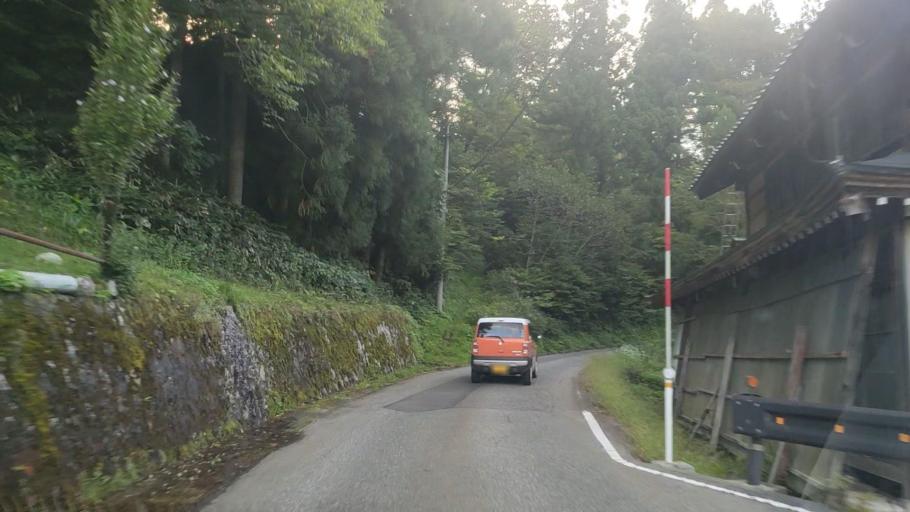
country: JP
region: Toyama
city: Yatsuomachi-higashikumisaka
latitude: 36.4806
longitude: 137.0744
